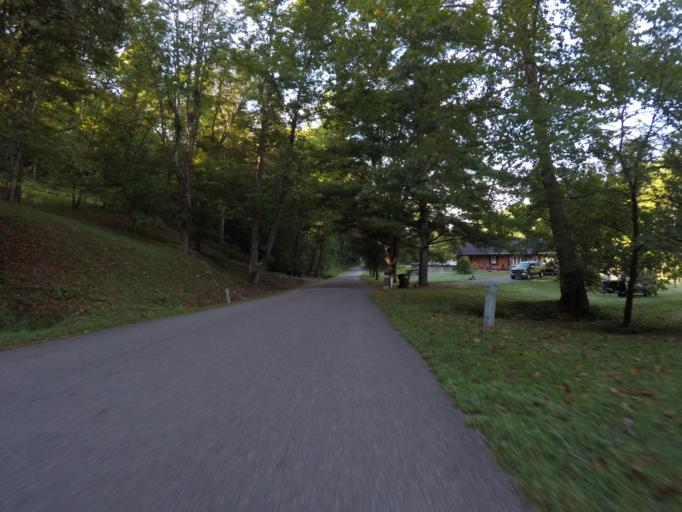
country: US
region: Ohio
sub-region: Lawrence County
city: Coal Grove
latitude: 38.5585
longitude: -82.5526
